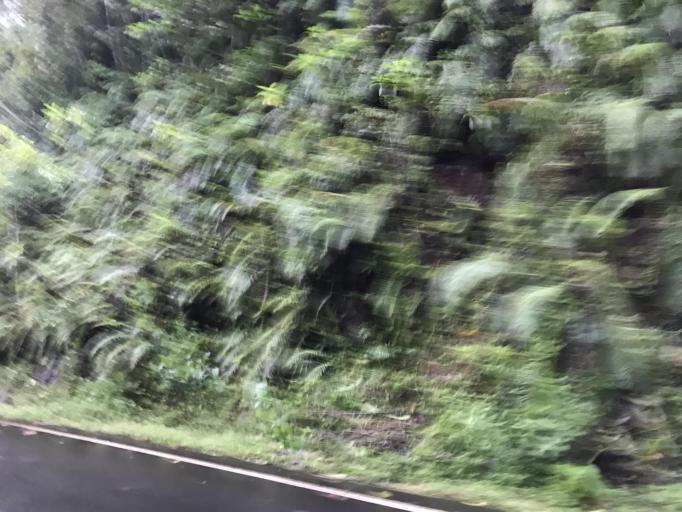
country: LK
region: Sabaragamuwa
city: Ratnapura
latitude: 6.5395
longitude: 80.3029
